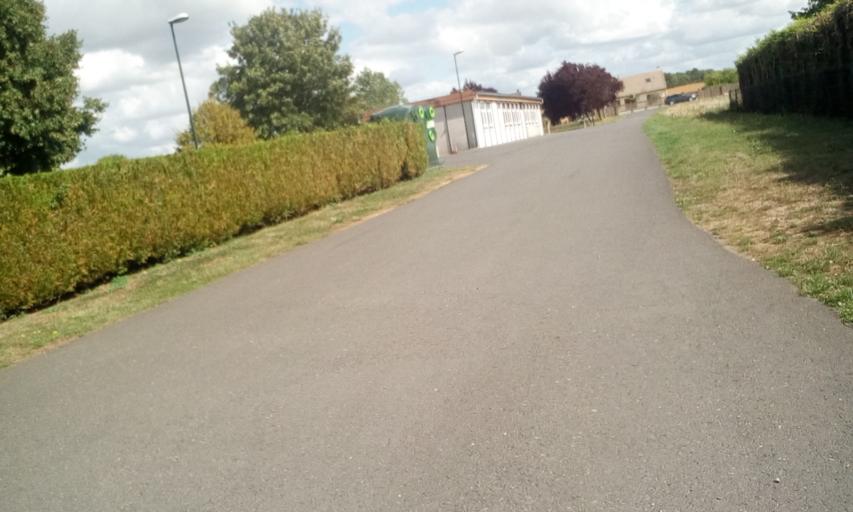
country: FR
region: Lower Normandy
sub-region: Departement du Calvados
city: Bellengreville
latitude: 49.0888
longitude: -0.1970
